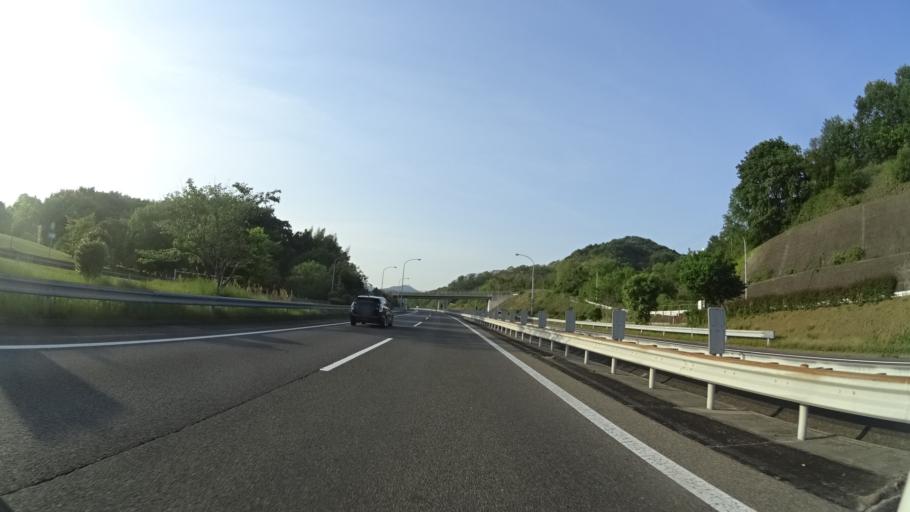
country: JP
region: Kagawa
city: Tadotsu
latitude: 34.1815
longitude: 133.7344
